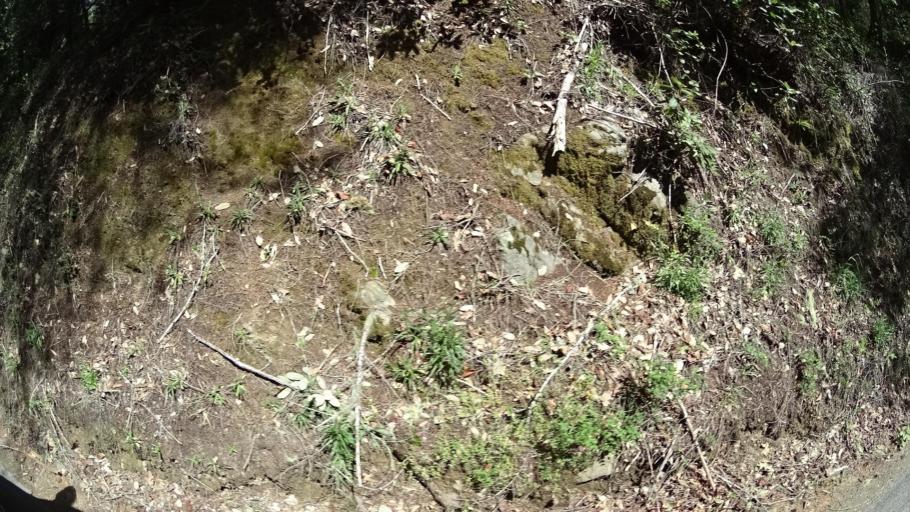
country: US
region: California
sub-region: Humboldt County
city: Redway
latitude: 40.2867
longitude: -123.6486
